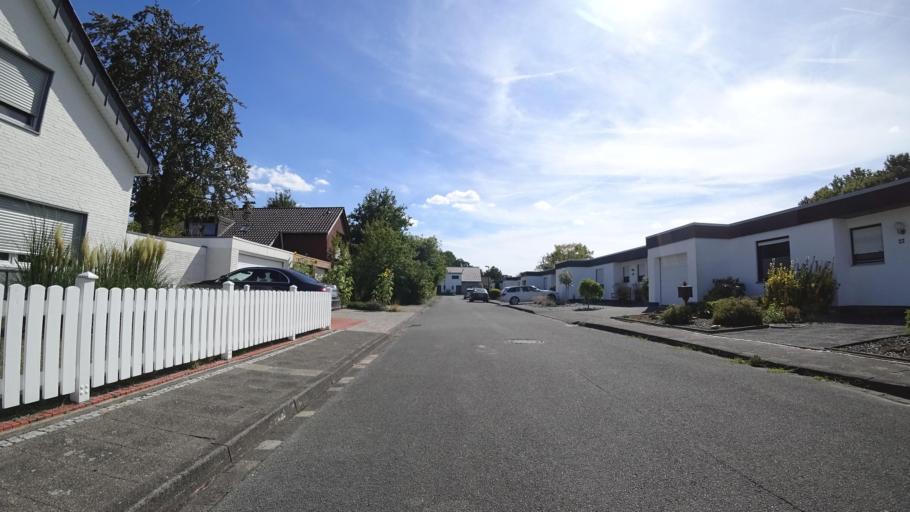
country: DE
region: North Rhine-Westphalia
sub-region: Regierungsbezirk Detmold
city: Guetersloh
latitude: 51.8920
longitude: 8.4008
